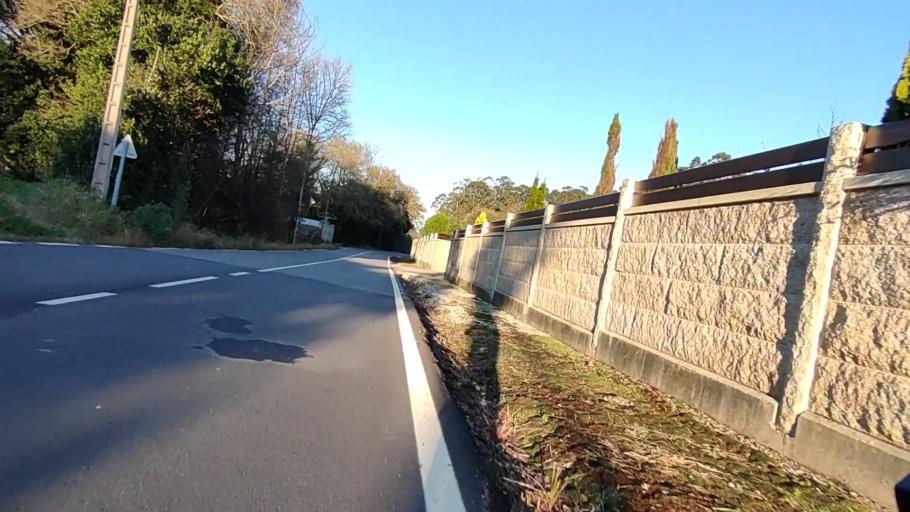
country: ES
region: Galicia
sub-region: Provincia da Coruna
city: Boiro
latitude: 42.6321
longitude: -8.8602
